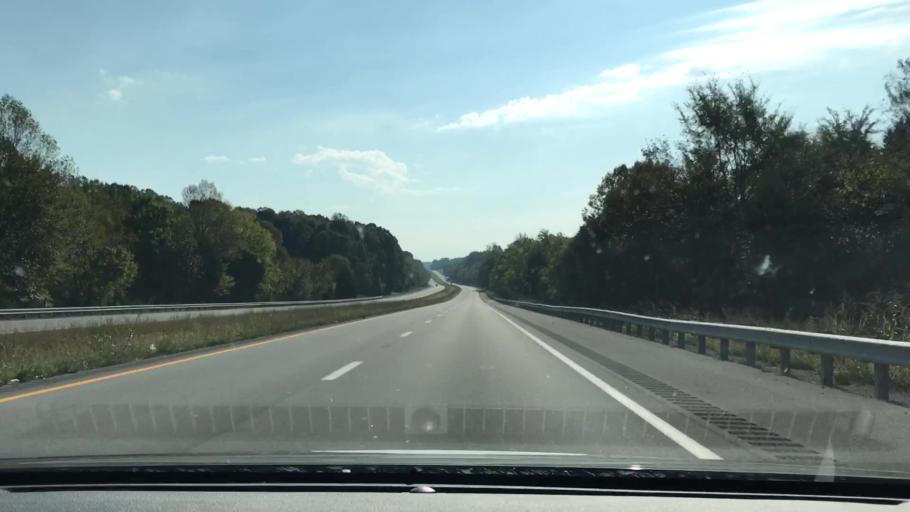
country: US
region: Kentucky
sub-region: Adair County
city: Columbia
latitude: 37.0673
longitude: -85.2041
